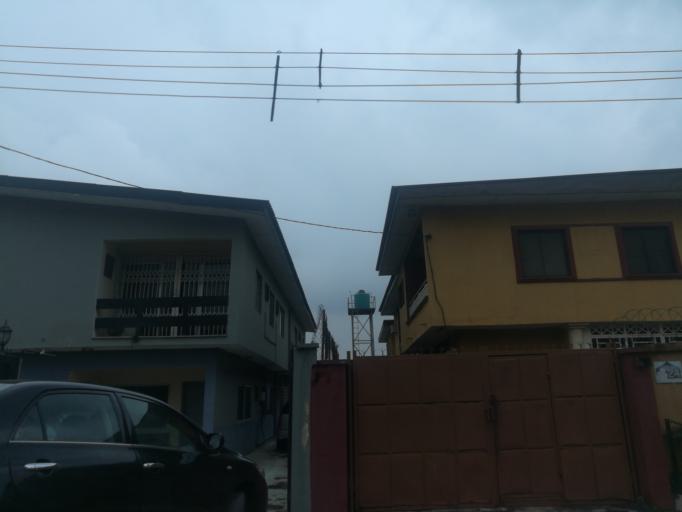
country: NG
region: Lagos
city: Ojota
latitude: 6.5686
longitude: 3.3753
